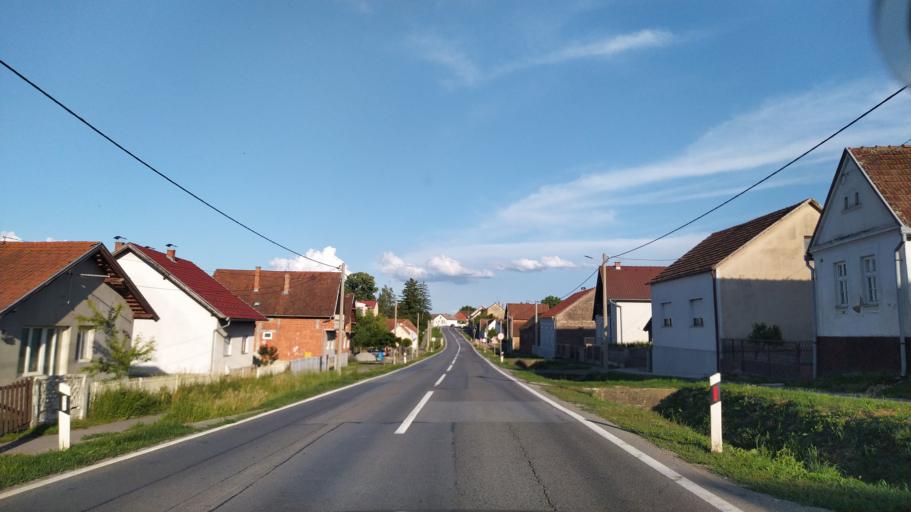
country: HR
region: Virovitick-Podravska
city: Slatina
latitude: 45.6649
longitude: 17.7667
